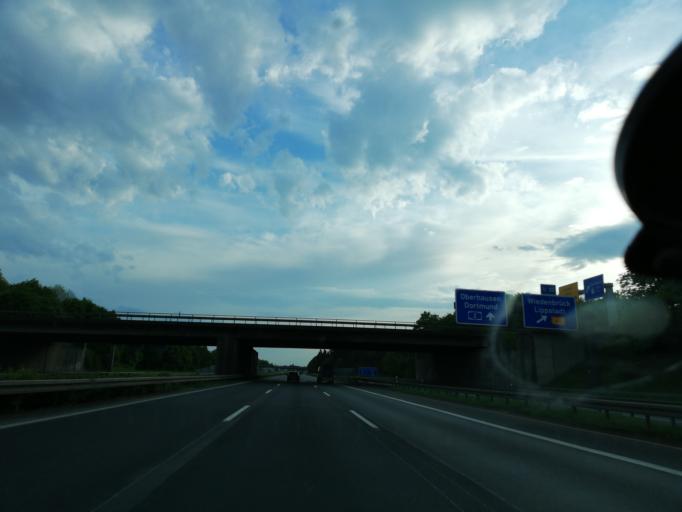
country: DE
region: North Rhine-Westphalia
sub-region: Regierungsbezirk Detmold
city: Rheda-Wiedenbruck
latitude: 51.8552
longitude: 8.3244
